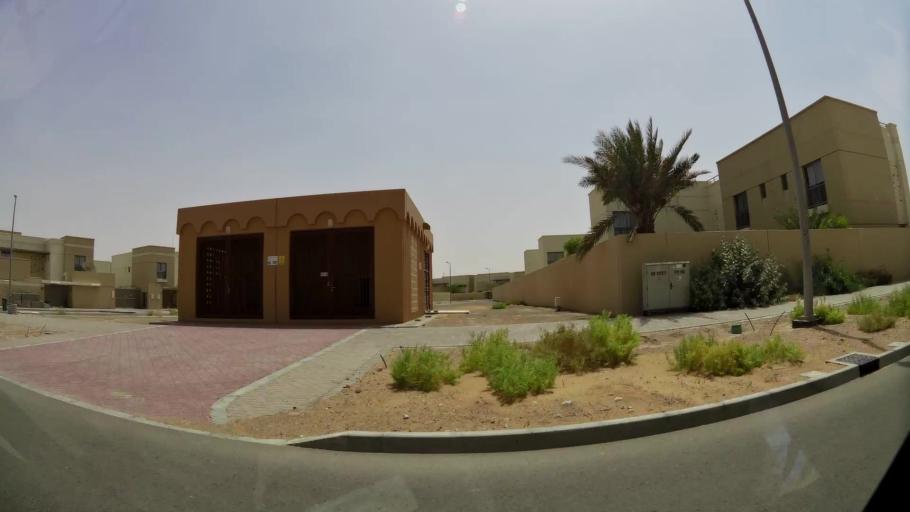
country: AE
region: Abu Dhabi
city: Al Ain
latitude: 24.1428
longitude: 55.6240
